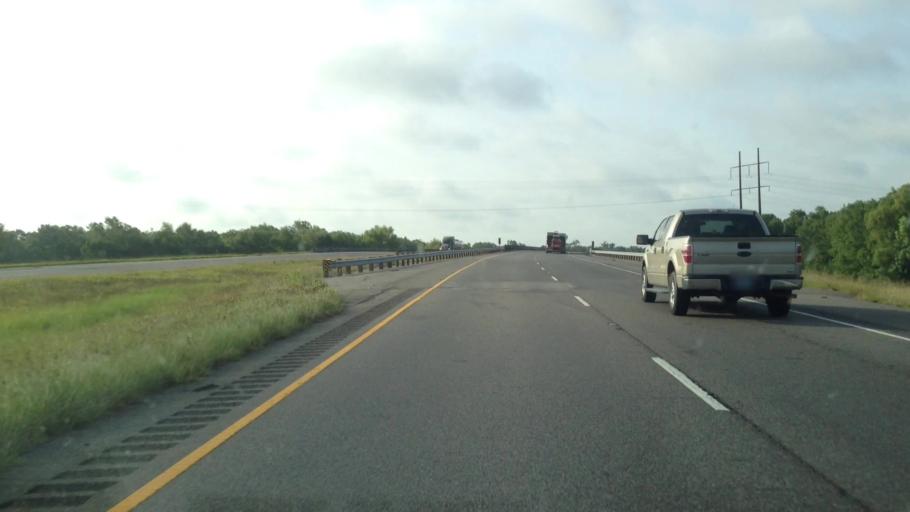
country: US
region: Louisiana
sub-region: Avoyelles Parish
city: Bunkie
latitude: 30.9007
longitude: -92.2301
